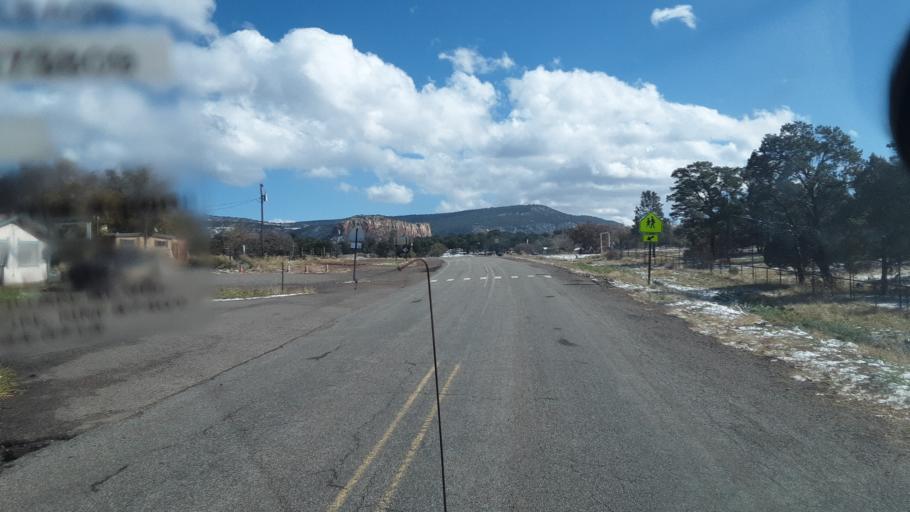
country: US
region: New Mexico
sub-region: Rio Arriba County
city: Santa Teresa
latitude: 36.2283
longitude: -106.8238
